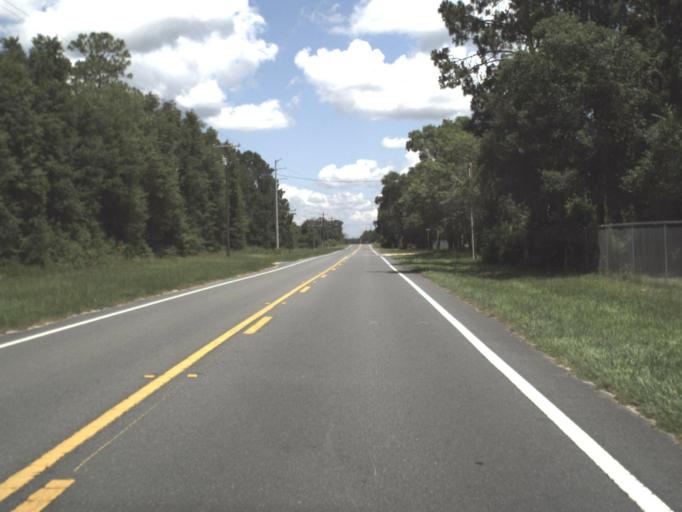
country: US
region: Florida
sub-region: Alachua County
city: Hawthorne
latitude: 29.6214
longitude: -82.0272
